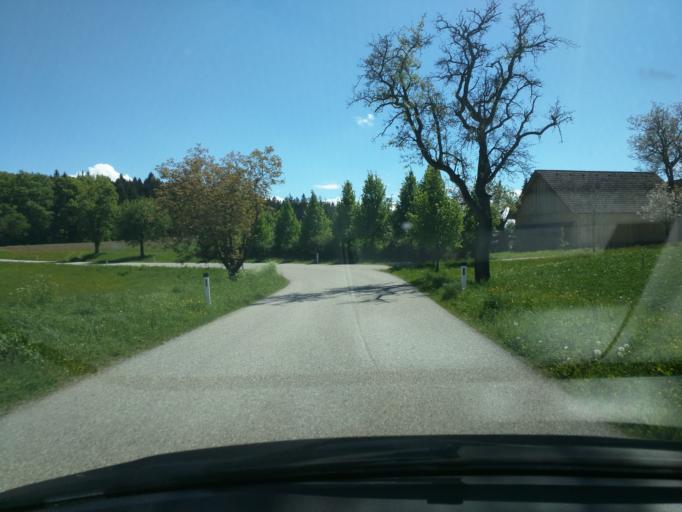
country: AT
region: Lower Austria
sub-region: Politischer Bezirk Melk
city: Blindenmarkt
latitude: 48.1611
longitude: 14.9706
